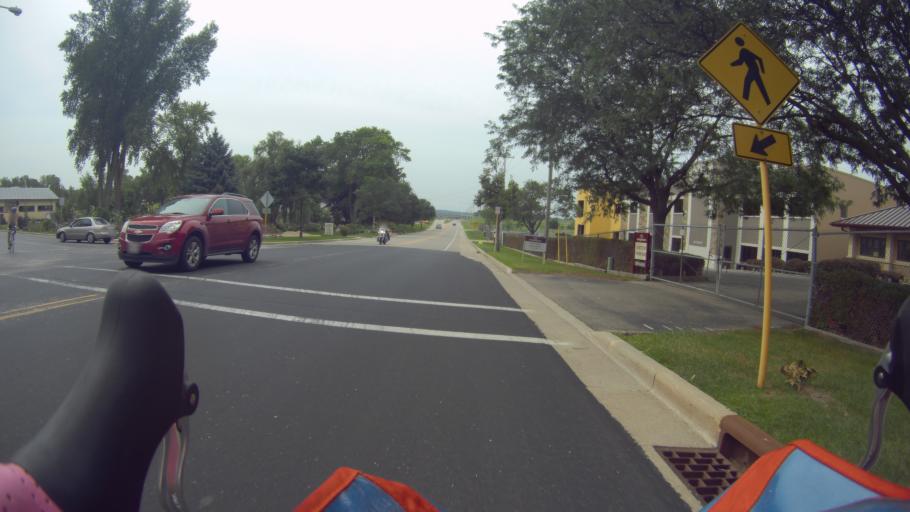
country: US
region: Wisconsin
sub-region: Dane County
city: Verona
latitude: 42.9793
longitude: -89.5417
